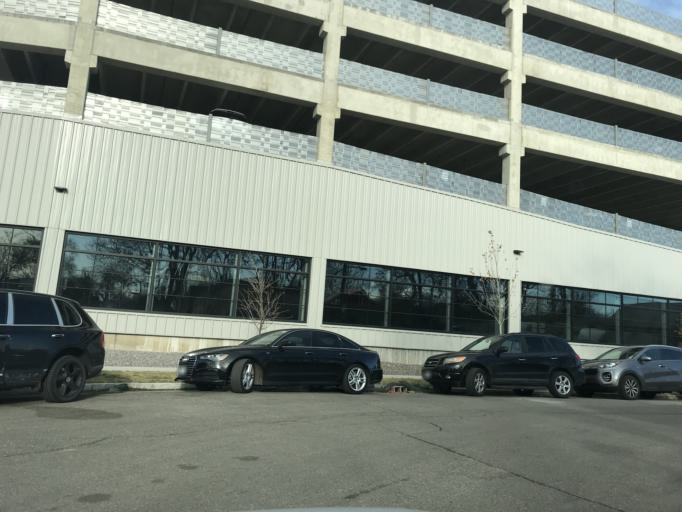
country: US
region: Colorado
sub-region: Denver County
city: Denver
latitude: 39.7697
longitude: -104.9700
